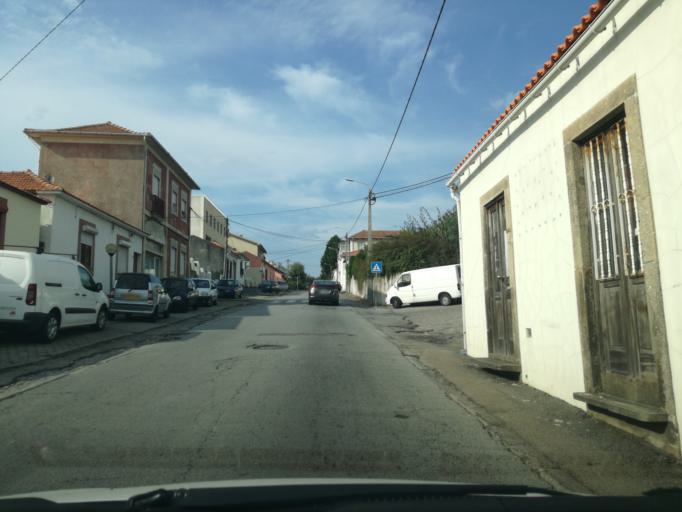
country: PT
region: Porto
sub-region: Vila Nova de Gaia
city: Azenha
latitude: 41.0638
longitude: -8.6282
